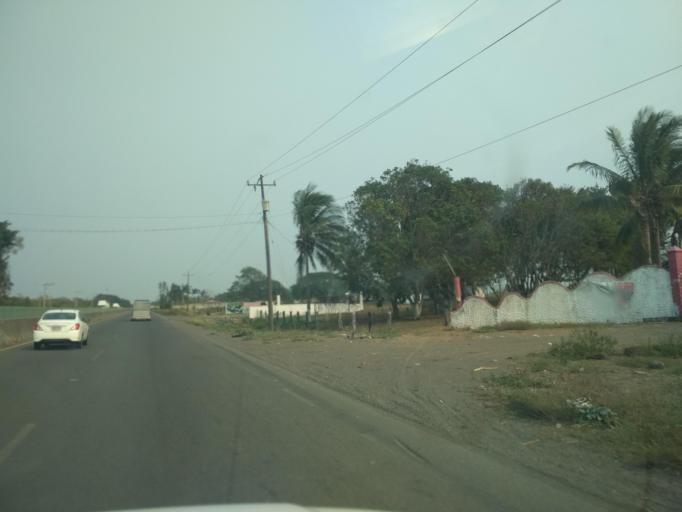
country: MX
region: Veracruz
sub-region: Veracruz
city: Hacienda Sotavento
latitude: 19.0920
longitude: -96.2061
